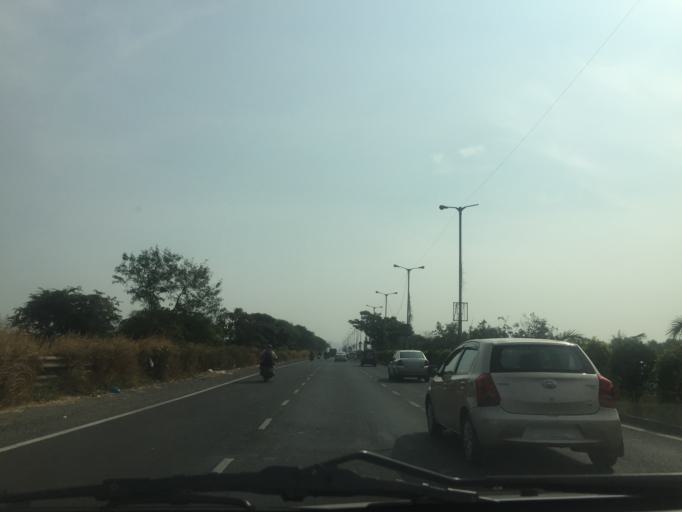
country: IN
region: Maharashtra
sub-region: Thane
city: Airoli
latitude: 19.1528
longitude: 72.9695
